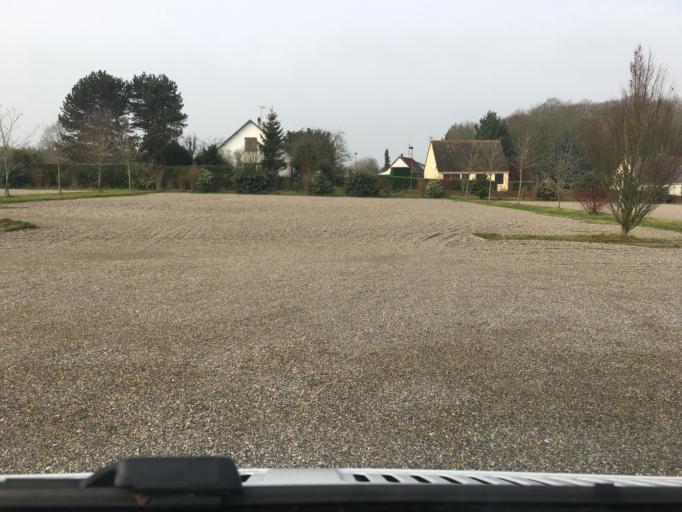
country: FR
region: Picardie
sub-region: Departement de la Somme
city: Saint-Valery-sur-Somme
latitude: 50.1829
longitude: 1.6286
